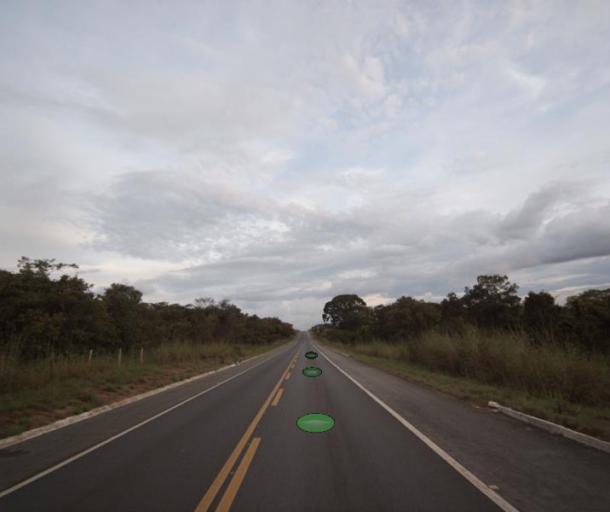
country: BR
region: Goias
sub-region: Barro Alto
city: Barro Alto
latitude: -15.1980
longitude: -48.7026
